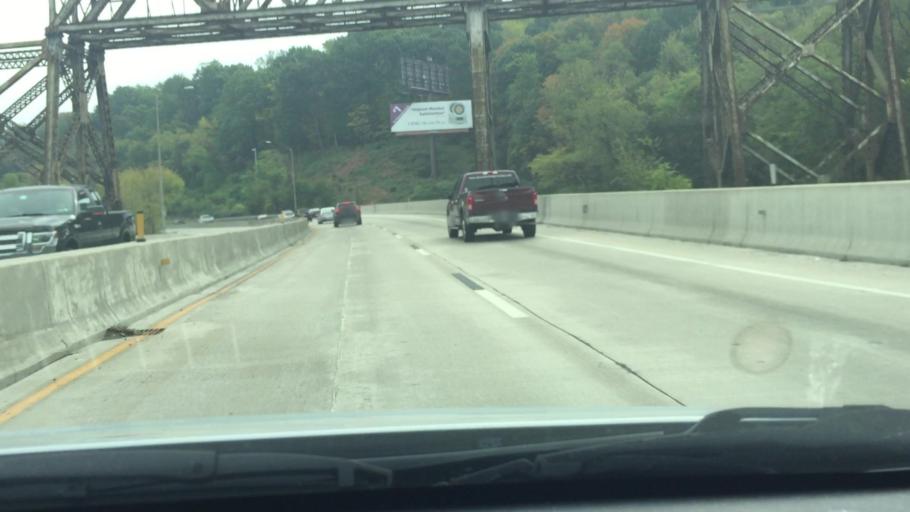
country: US
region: Pennsylvania
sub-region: Allegheny County
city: Carnegie
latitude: 40.4109
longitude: -80.0743
